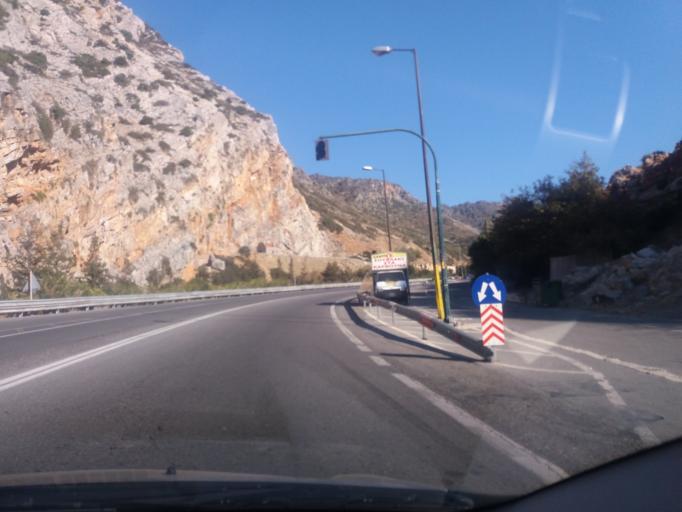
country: GR
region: Crete
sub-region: Nomos Lasithiou
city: Sision
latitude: 35.2850
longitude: 25.5420
